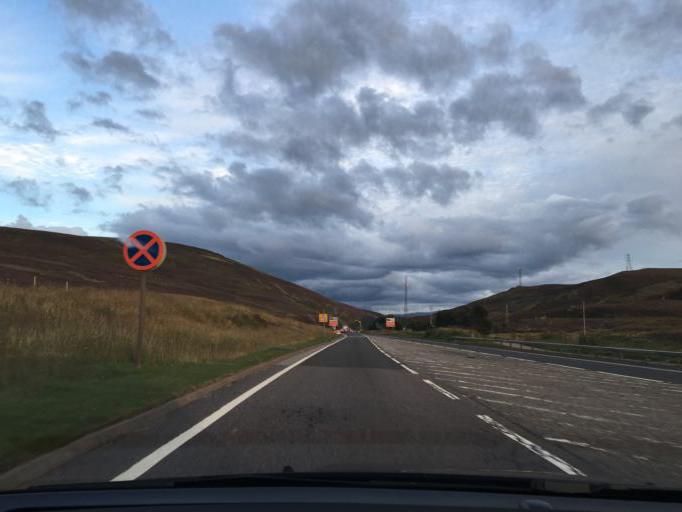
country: GB
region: Scotland
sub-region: Highland
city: Aviemore
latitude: 57.3093
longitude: -3.9413
